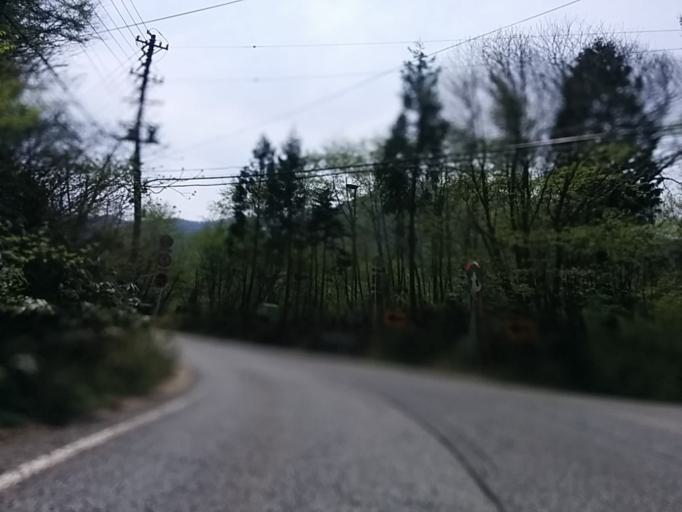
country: JP
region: Gifu
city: Takayama
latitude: 36.2218
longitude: 137.5415
